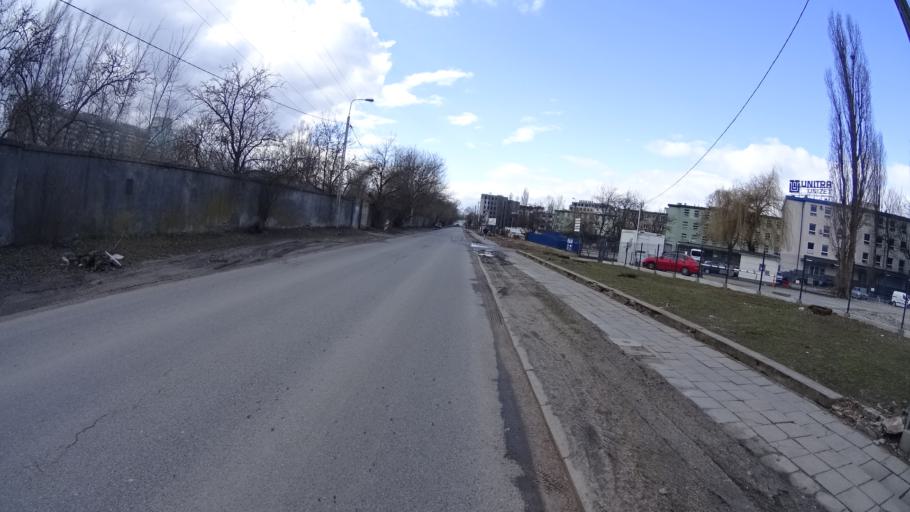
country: PL
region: Masovian Voivodeship
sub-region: Warszawa
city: Ochota
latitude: 52.2244
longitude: 20.9758
